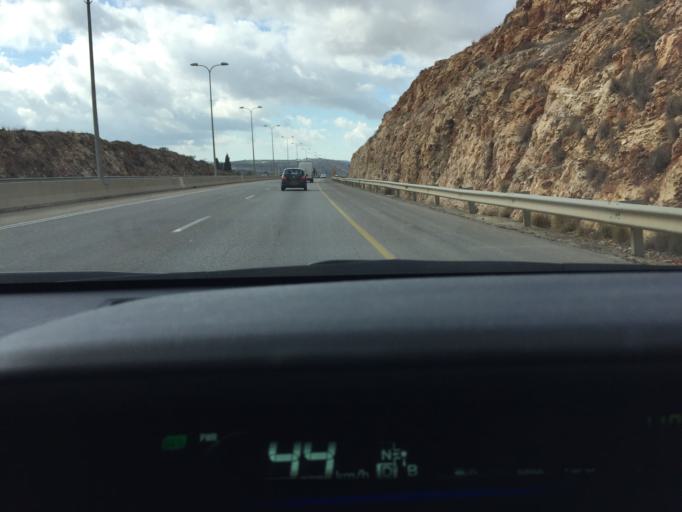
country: IL
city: Revava
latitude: 32.1022
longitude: 35.1245
